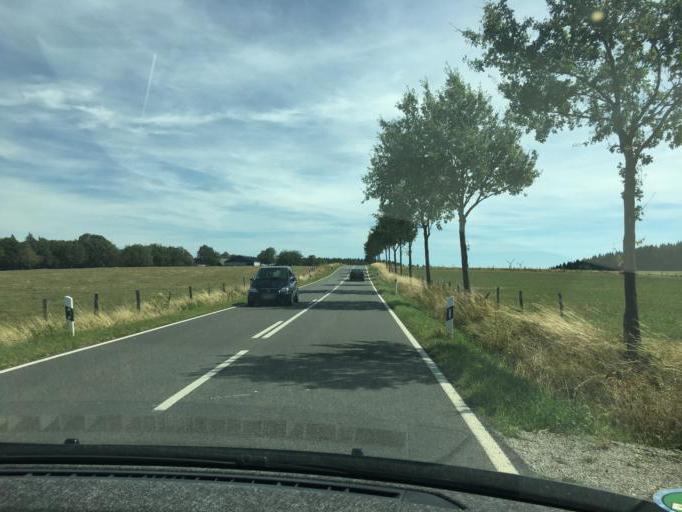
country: DE
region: North Rhine-Westphalia
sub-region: Regierungsbezirk Koln
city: Hurtgenwald
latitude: 50.6693
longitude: 6.3276
